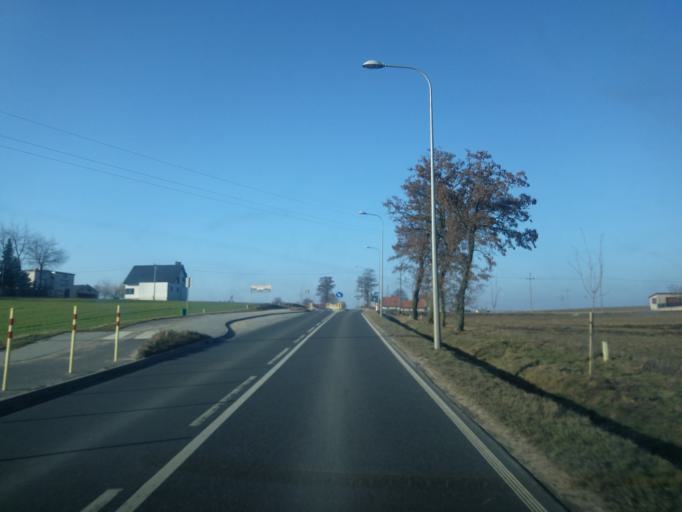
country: PL
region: Warmian-Masurian Voivodeship
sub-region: Powiat ilawski
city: Lubawa
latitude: 53.4628
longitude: 19.7740
